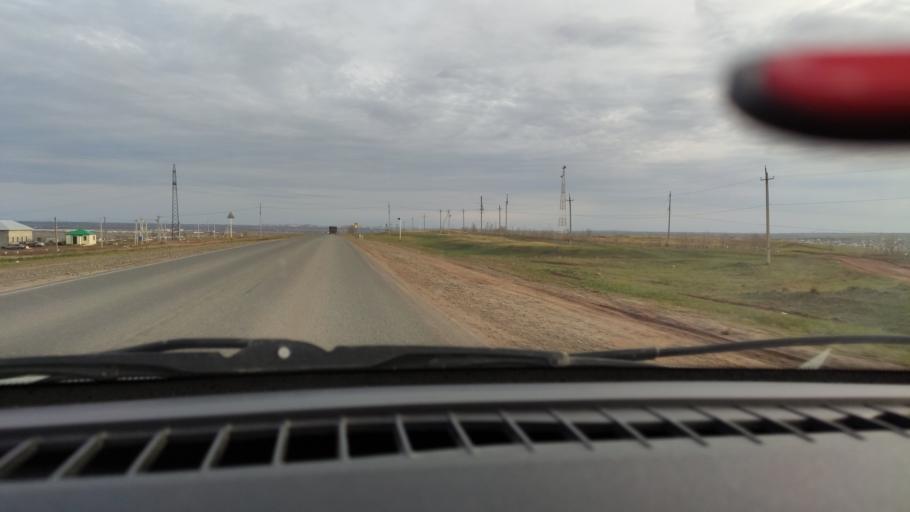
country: RU
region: Orenburg
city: Tatarskaya Kargala
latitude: 51.9602
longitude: 55.1840
